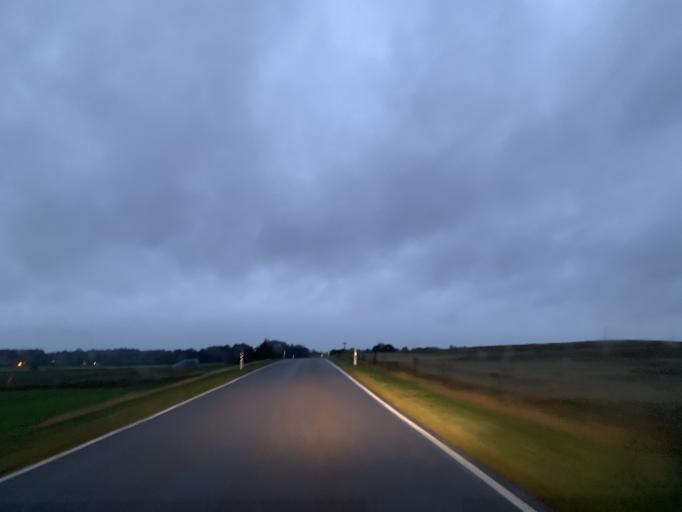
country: DE
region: Schleswig-Holstein
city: Nebel
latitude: 54.6399
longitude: 8.3681
